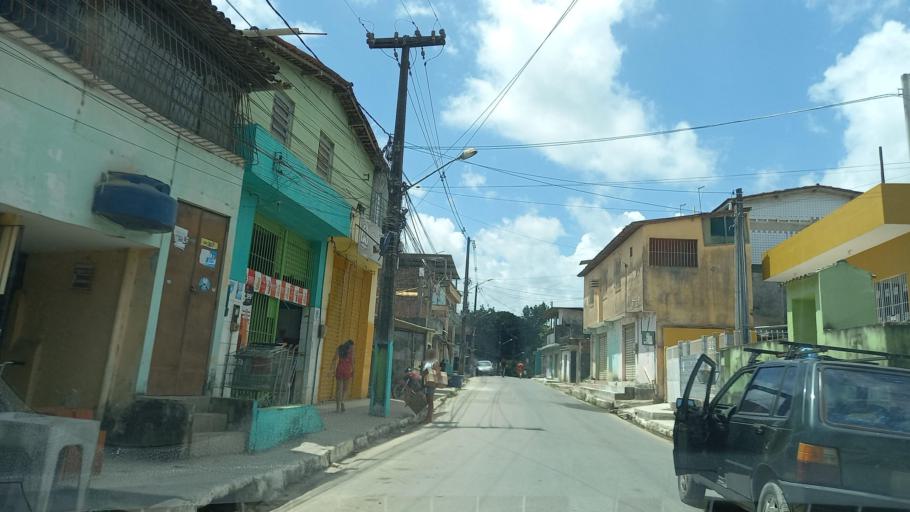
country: BR
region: Pernambuco
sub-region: Jaboatao Dos Guararapes
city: Jaboatao
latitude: -8.1736
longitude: -35.0010
